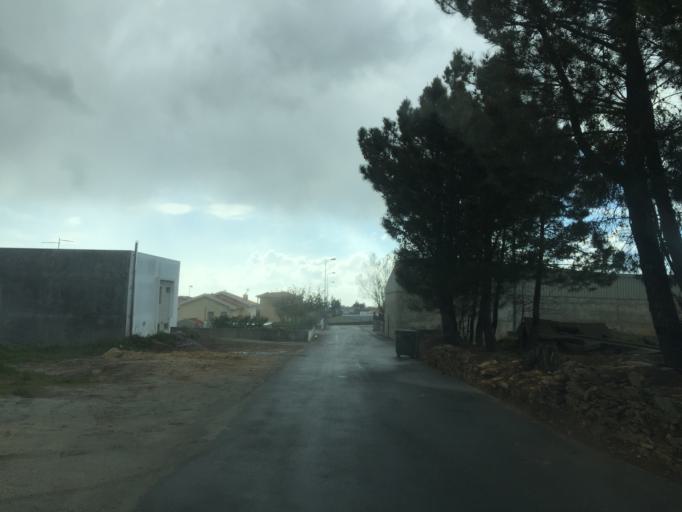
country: PT
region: Braganca
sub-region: Mogadouro
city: Mogadouro
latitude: 41.3430
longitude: -6.7006
